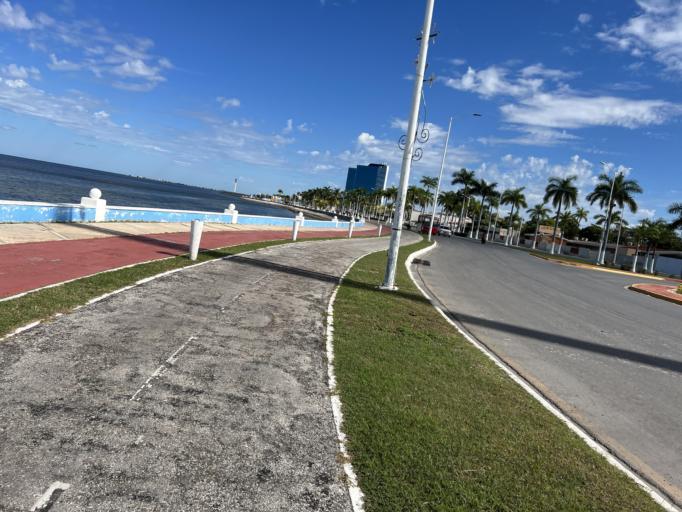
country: MX
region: Campeche
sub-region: Campeche
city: Campeche
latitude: 19.8422
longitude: -90.5460
